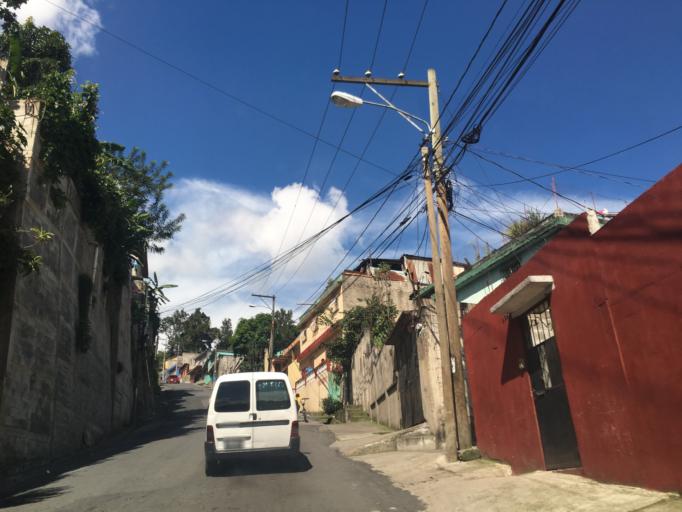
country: GT
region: Guatemala
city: Mixco
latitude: 14.6257
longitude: -90.5828
